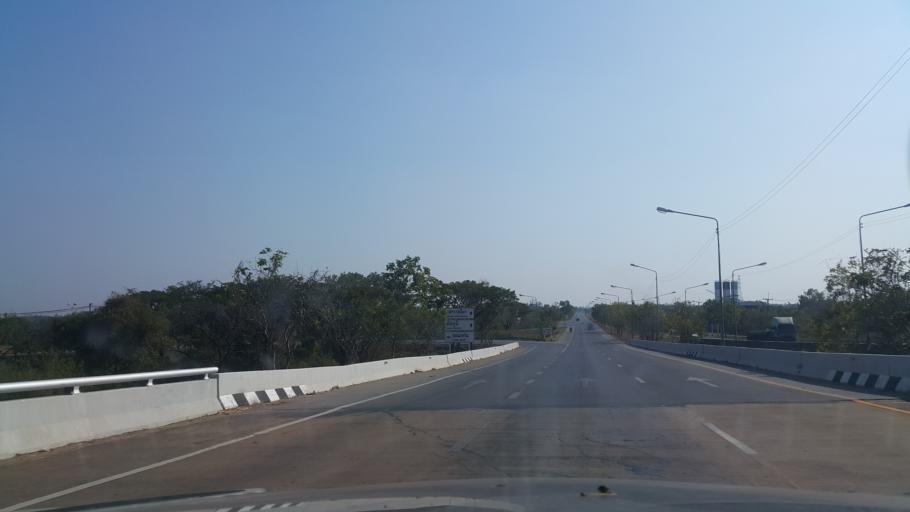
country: TH
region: Khon Kaen
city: Khon Kaen
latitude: 16.4365
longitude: 102.9179
